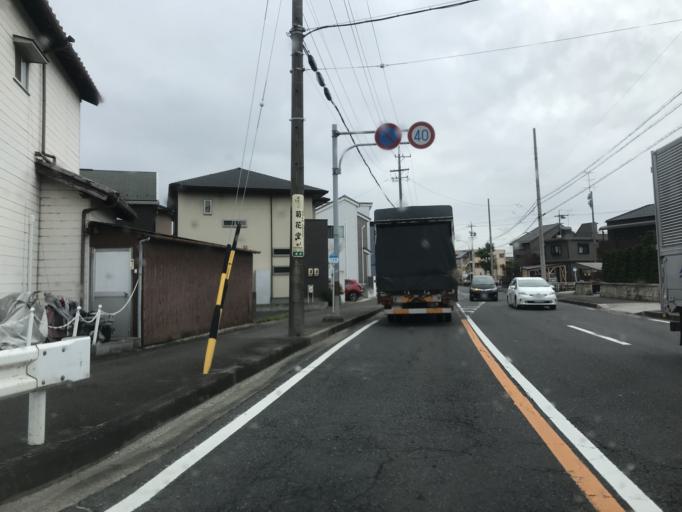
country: JP
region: Aichi
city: Inazawa
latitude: 35.2092
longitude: 136.8408
